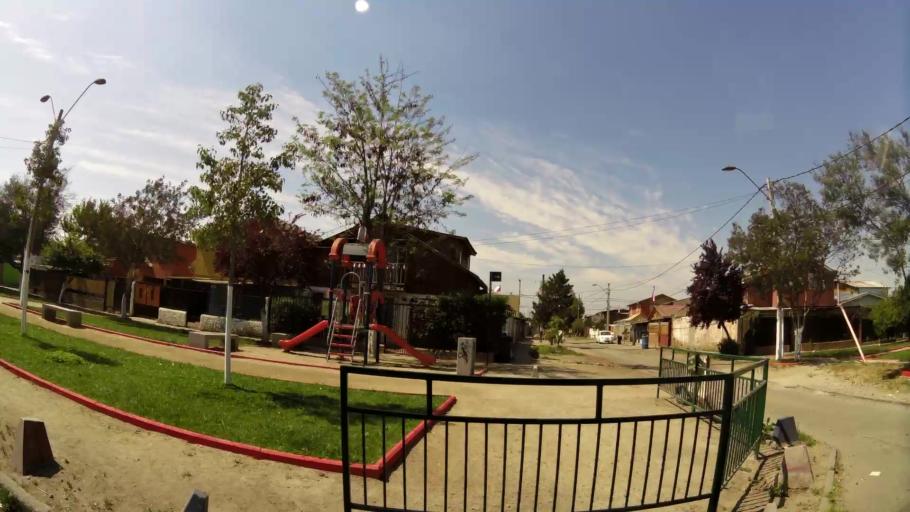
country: CL
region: Santiago Metropolitan
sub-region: Provincia de Santiago
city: La Pintana
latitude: -33.5465
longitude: -70.6367
